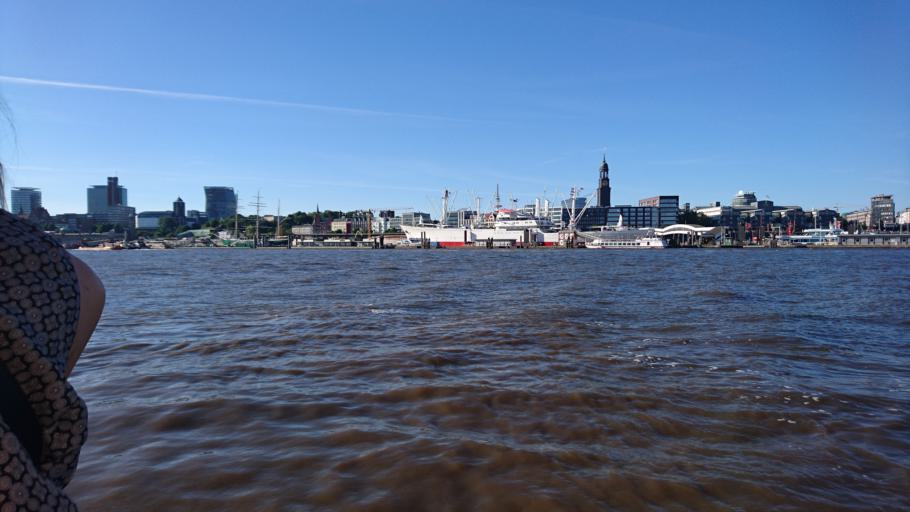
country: DE
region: Hamburg
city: Neustadt
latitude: 53.5403
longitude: 9.9761
